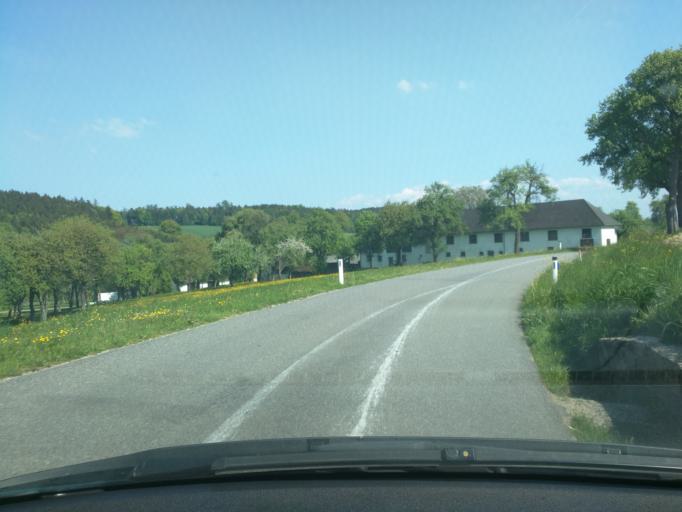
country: AT
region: Lower Austria
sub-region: Politischer Bezirk Melk
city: Blindenmarkt
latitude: 48.1406
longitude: 14.9885
